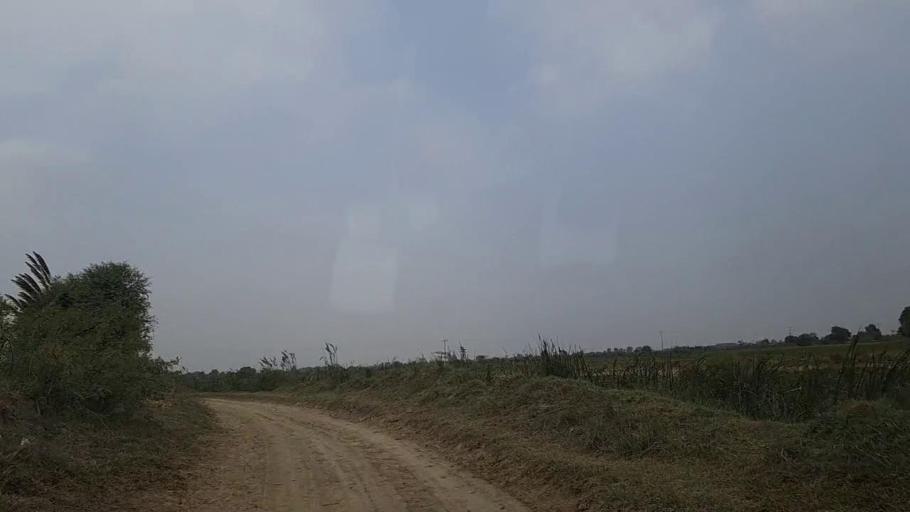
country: PK
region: Sindh
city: Mirpur Sakro
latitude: 24.6073
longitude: 67.7067
